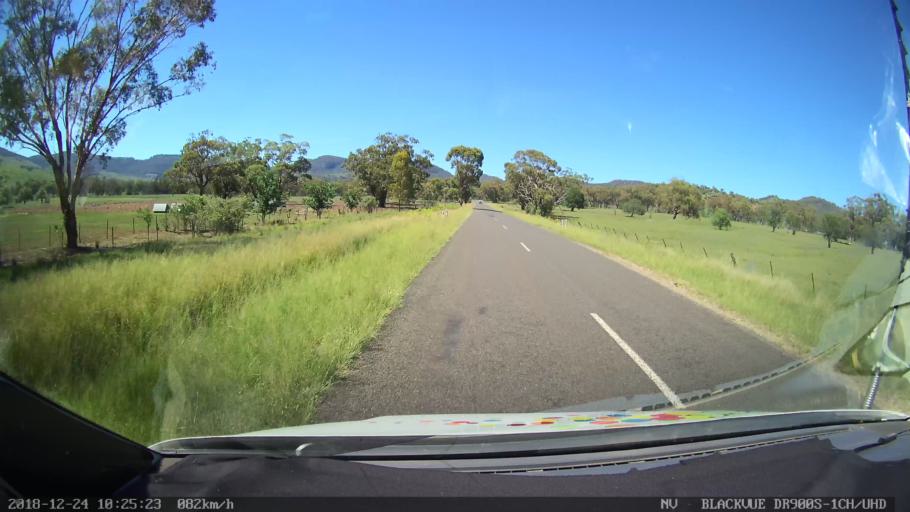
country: AU
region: New South Wales
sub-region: Liverpool Plains
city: Quirindi
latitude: -31.7983
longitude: 150.5287
